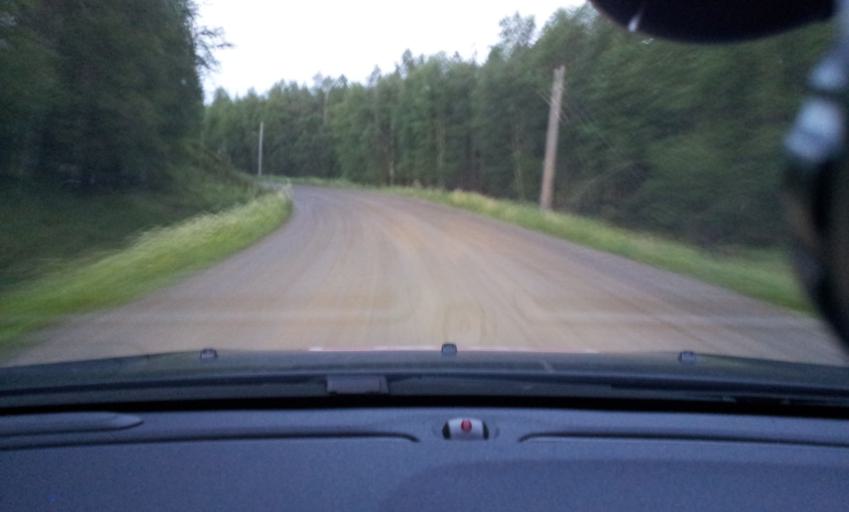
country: SE
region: Vaesternorrland
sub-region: Ange Kommun
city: Fransta
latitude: 62.7903
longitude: 16.0418
